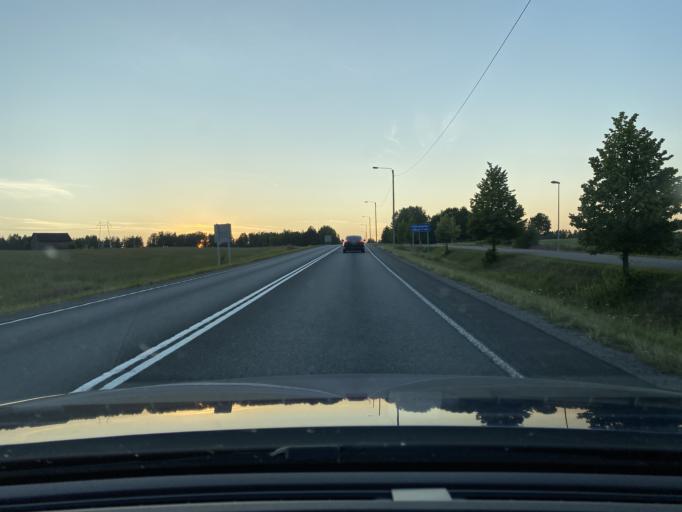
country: FI
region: Pirkanmaa
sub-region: Luoteis-Pirkanmaa
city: Ikaalinen
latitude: 61.7611
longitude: 23.0247
